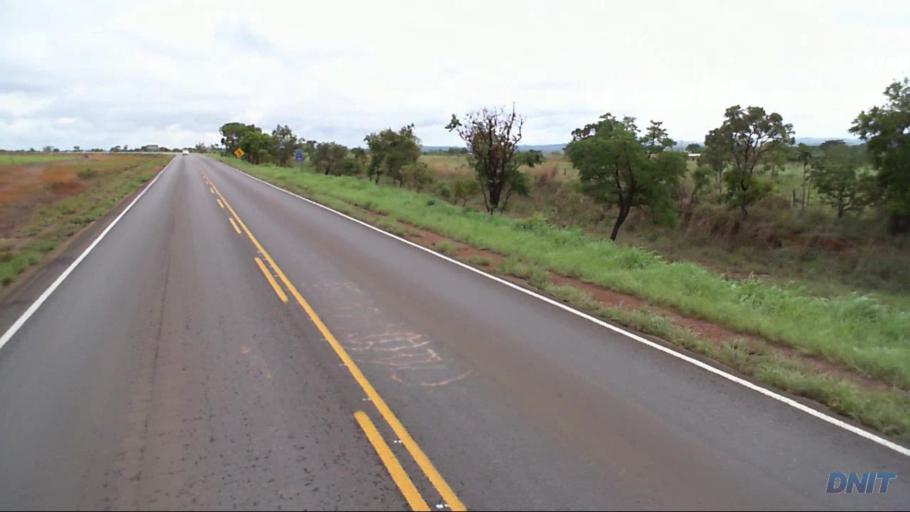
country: BR
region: Goias
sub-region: Padre Bernardo
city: Padre Bernardo
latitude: -15.3117
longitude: -48.2276
